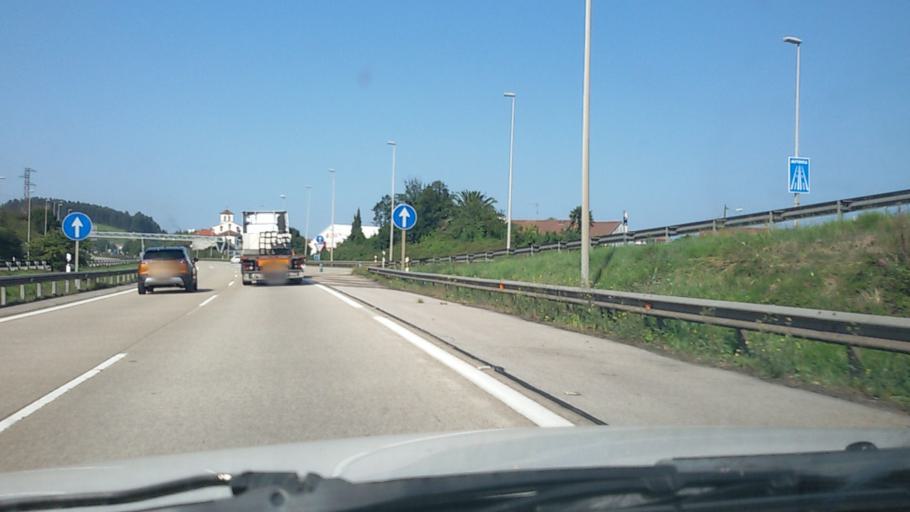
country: ES
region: Asturias
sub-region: Province of Asturias
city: Corvera de Asturias
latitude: 43.5498
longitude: -5.8709
